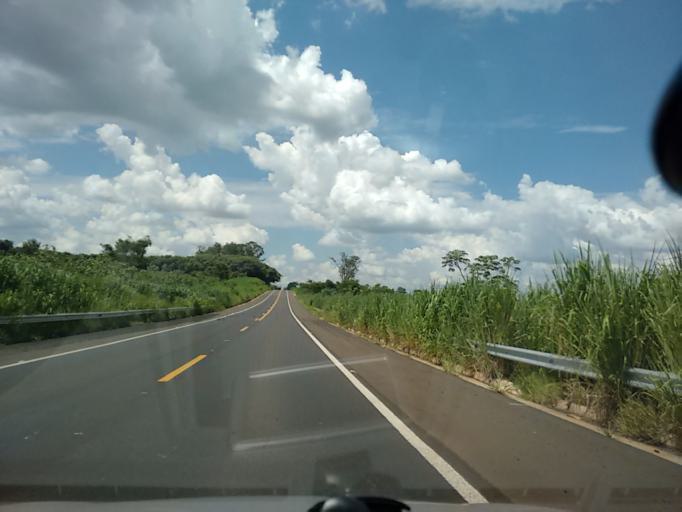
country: BR
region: Sao Paulo
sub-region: Osvaldo Cruz
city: Osvaldo Cruz
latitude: -21.8831
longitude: -50.8663
